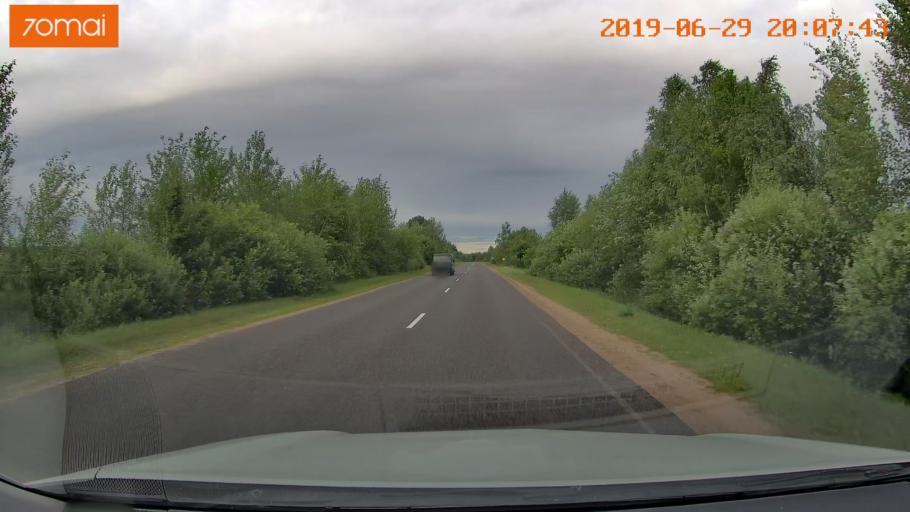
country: BY
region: Brest
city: Lahishyn
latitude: 52.3417
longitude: 26.0422
